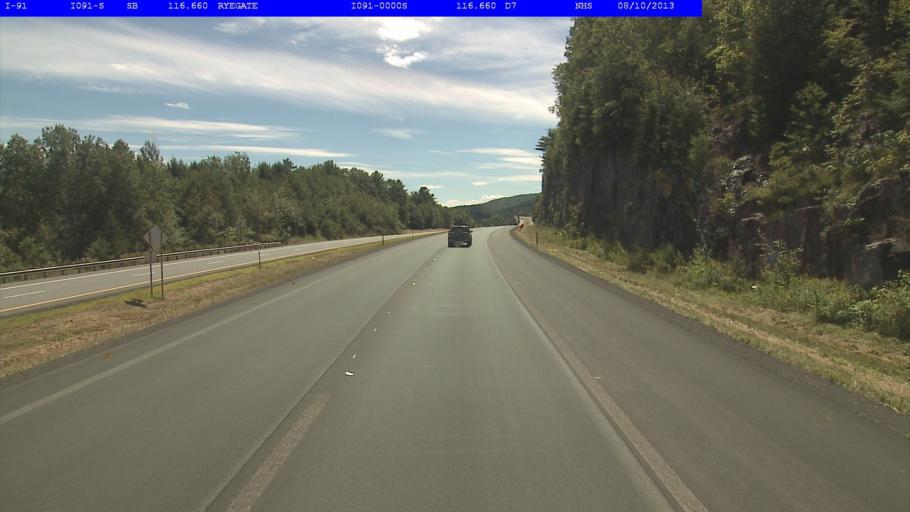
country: US
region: New Hampshire
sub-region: Grafton County
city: Woodsville
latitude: 44.2478
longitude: -72.0619
